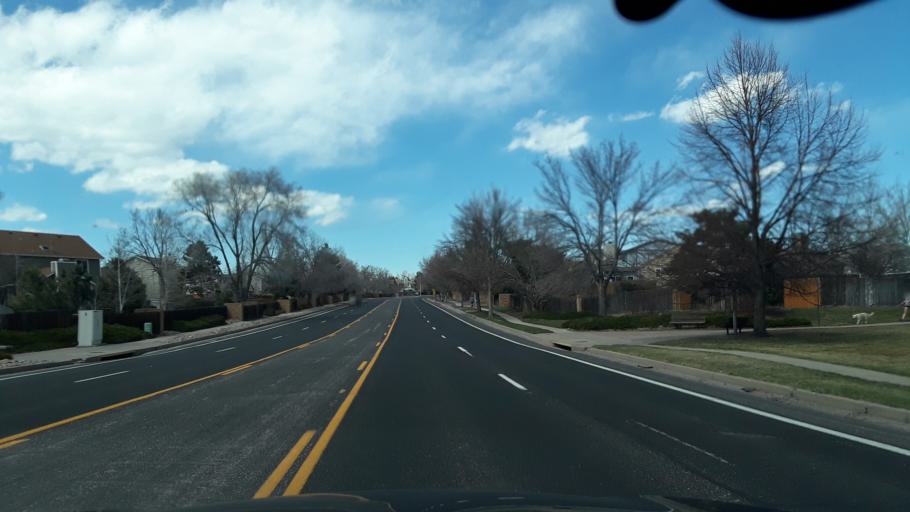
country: US
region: Colorado
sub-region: El Paso County
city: Black Forest
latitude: 38.9519
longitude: -104.7512
